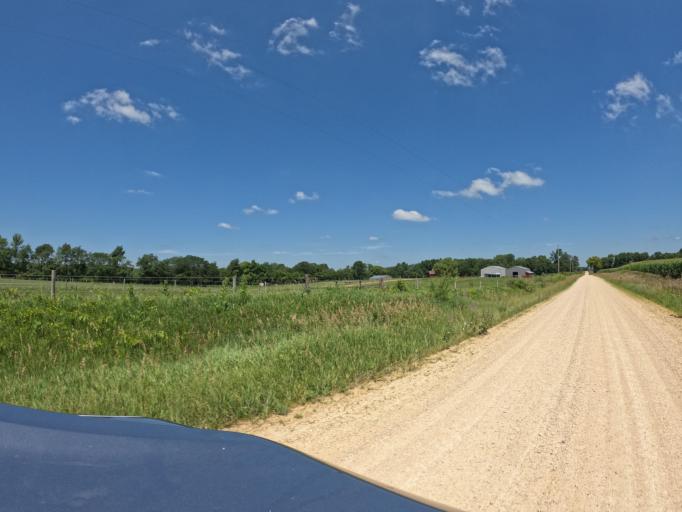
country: US
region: Iowa
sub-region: Clinton County
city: De Witt
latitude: 41.7640
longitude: -90.4325
